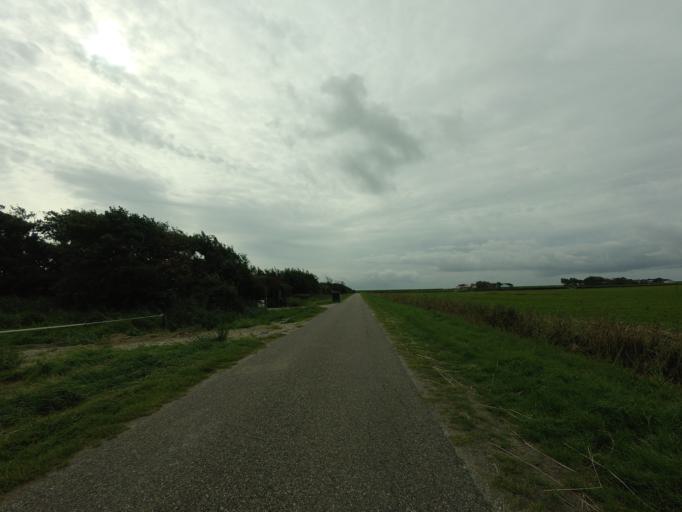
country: NL
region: Friesland
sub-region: Gemeente Ameland
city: Nes
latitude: 53.4377
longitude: 5.7069
